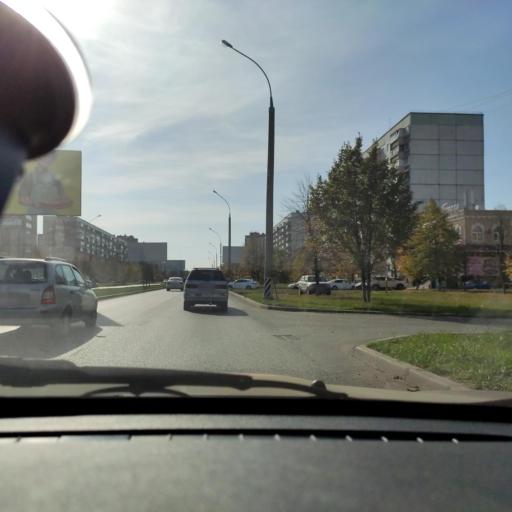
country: RU
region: Samara
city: Tol'yatti
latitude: 53.5467
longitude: 49.3317
